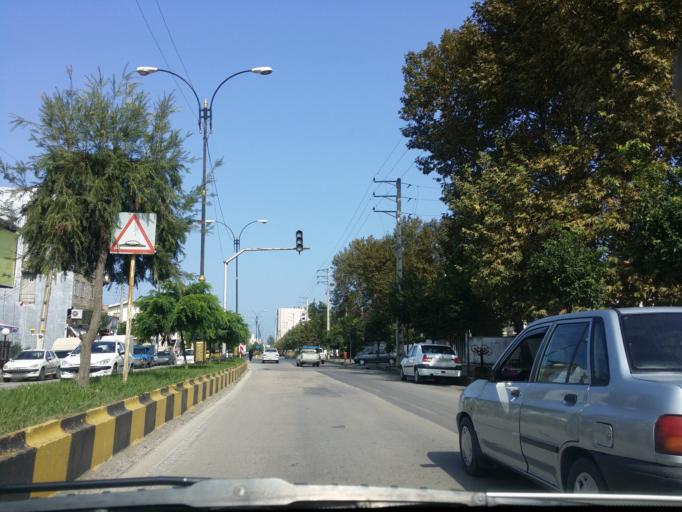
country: IR
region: Mazandaran
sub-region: Nowshahr
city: Nowshahr
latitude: 36.6408
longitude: 51.4904
